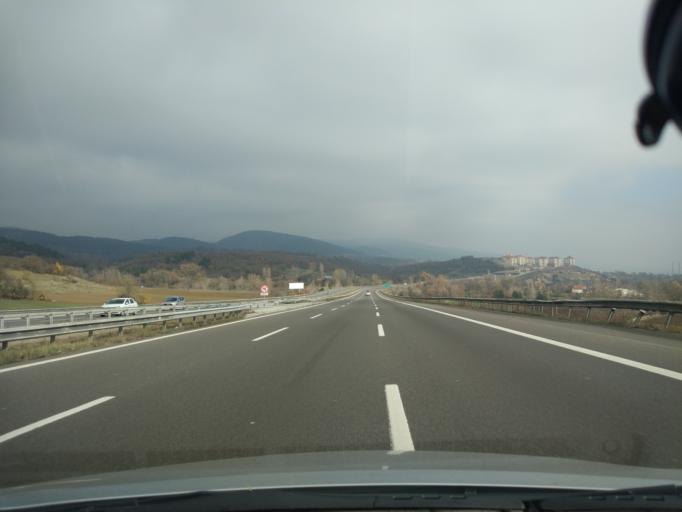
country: TR
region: Bolu
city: Bolu
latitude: 40.7352
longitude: 31.5332
